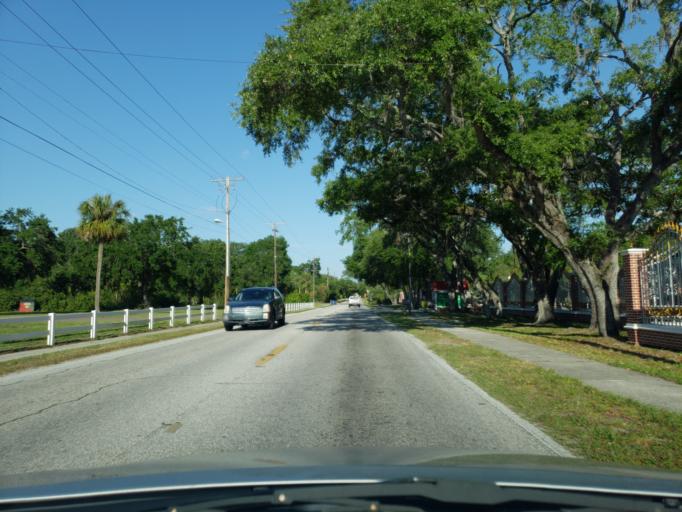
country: US
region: Florida
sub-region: Hillsborough County
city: Palm River-Clair Mel
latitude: 27.9431
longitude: -82.3946
